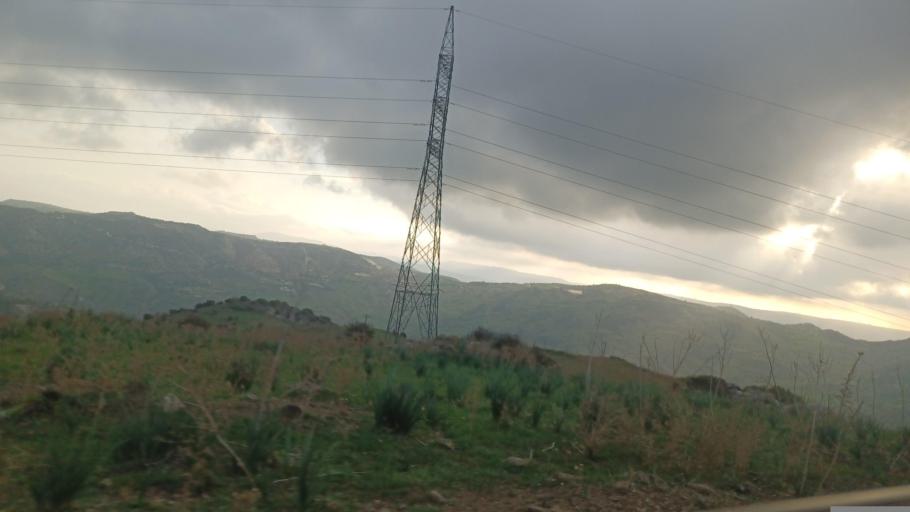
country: CY
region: Pafos
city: Mesogi
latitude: 34.7852
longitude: 32.5110
